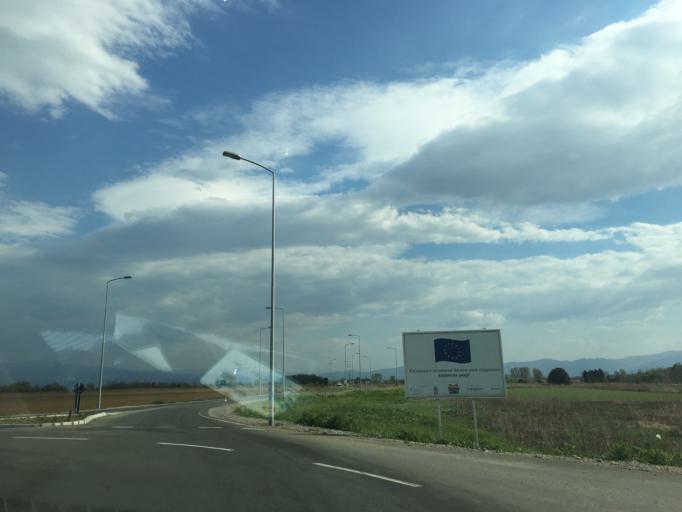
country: RS
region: Central Serbia
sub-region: Jablanicki Okrug
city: Leskovac
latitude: 43.0281
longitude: 21.9441
